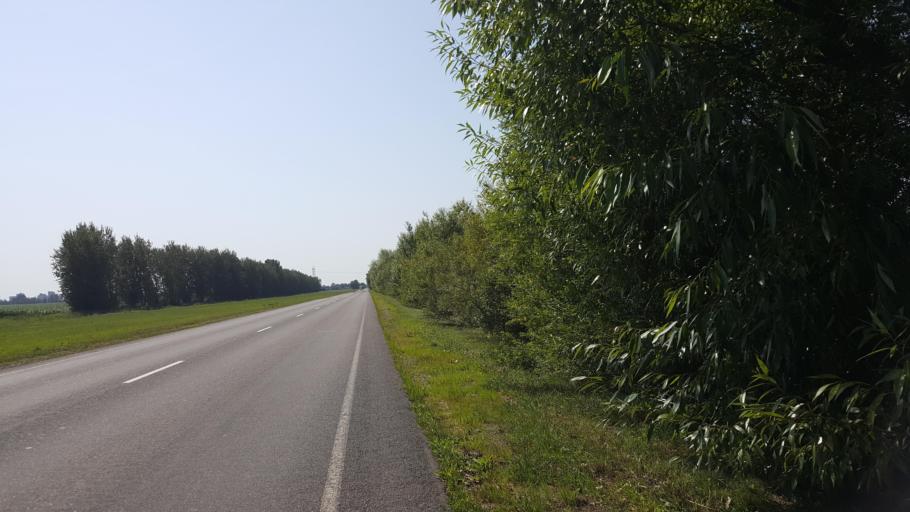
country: BY
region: Brest
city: Zhabinka
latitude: 52.2200
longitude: 23.9931
